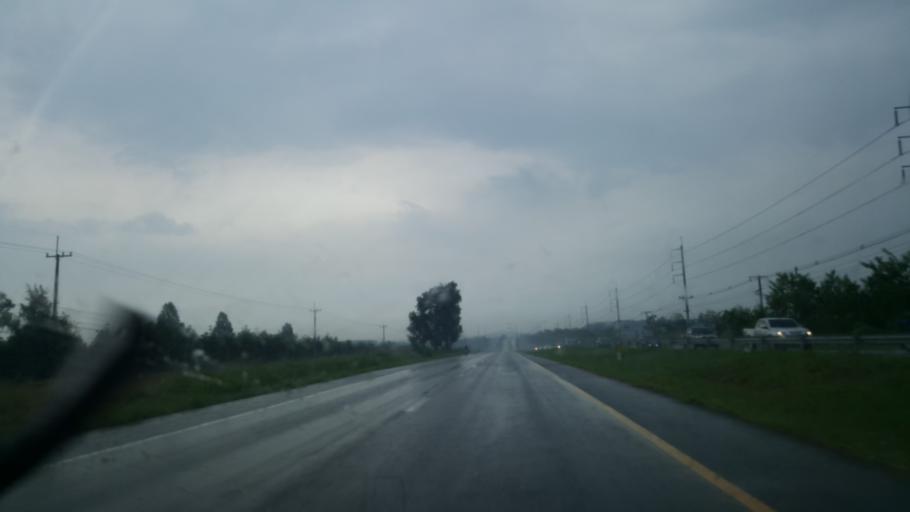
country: TH
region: Chon Buri
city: Ban Talat Bueng
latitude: 12.9777
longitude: 101.0583
